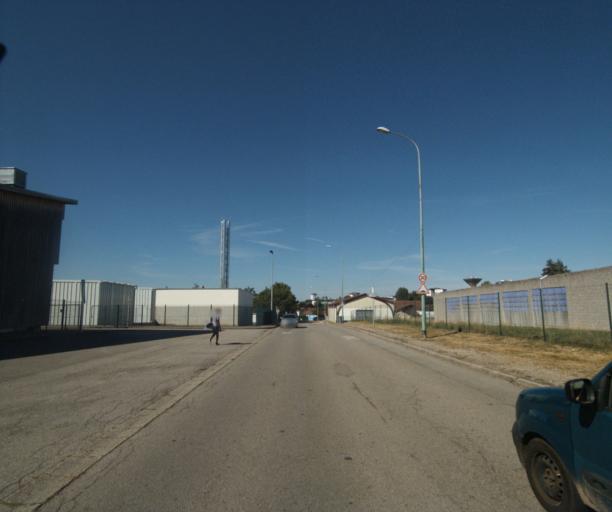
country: FR
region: Lorraine
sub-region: Departement des Vosges
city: Epinal
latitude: 48.1862
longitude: 6.4687
